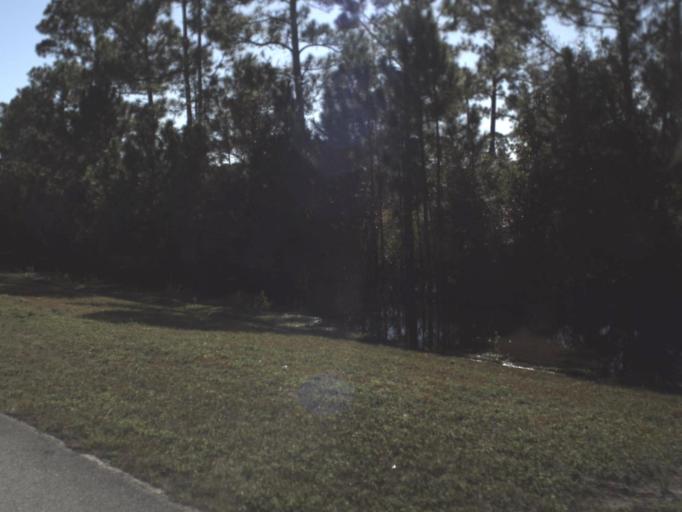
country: US
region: Florida
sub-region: Volusia County
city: South Daytona
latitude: 29.1635
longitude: -81.0707
